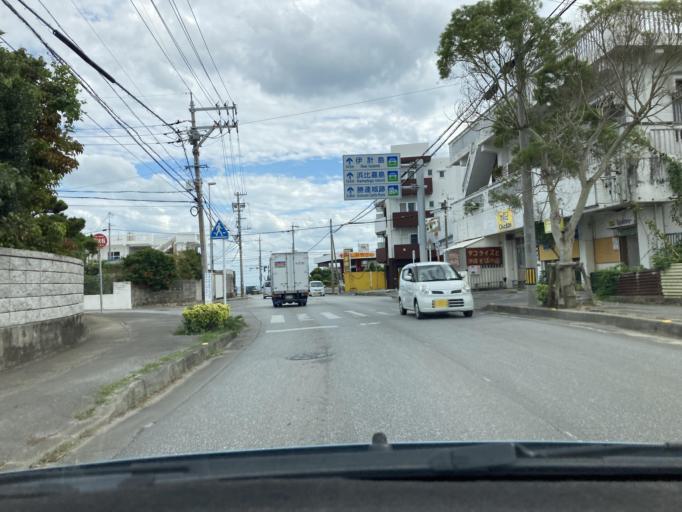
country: JP
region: Okinawa
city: Gushikawa
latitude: 26.3508
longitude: 127.8366
